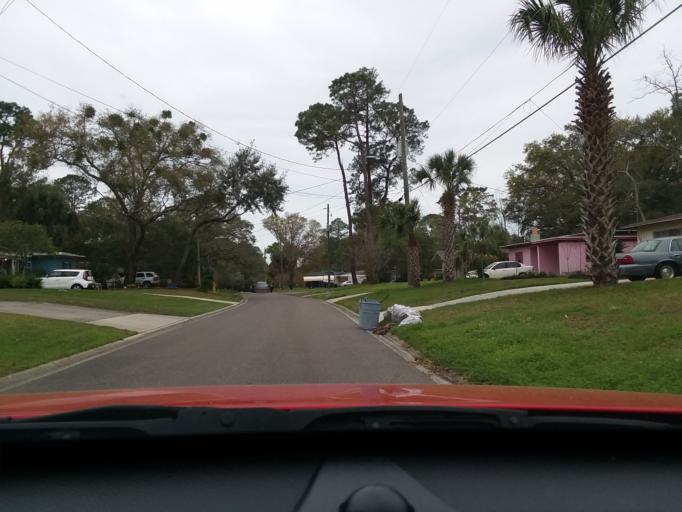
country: US
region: Florida
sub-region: Duval County
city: Jacksonville
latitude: 30.2849
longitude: -81.7337
